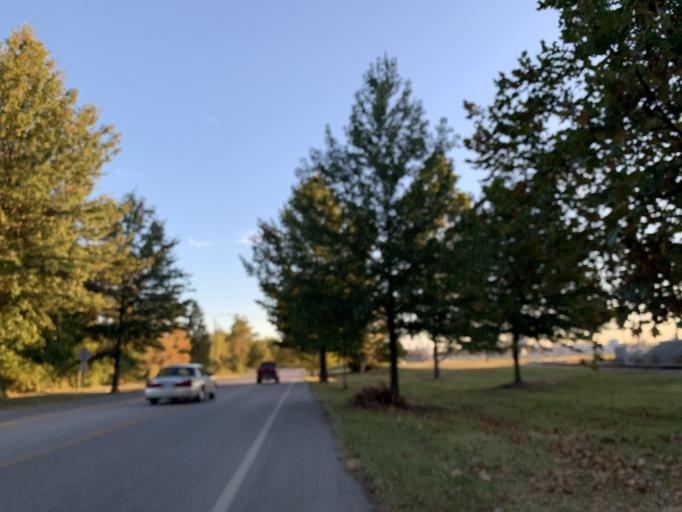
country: US
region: Kentucky
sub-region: Jefferson County
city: Shively
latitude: 38.2301
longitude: -85.8277
